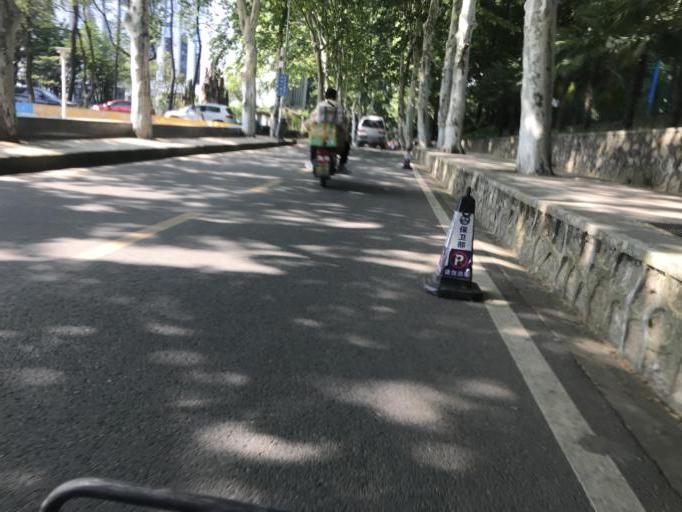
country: CN
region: Hubei
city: Shizishan
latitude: 30.5306
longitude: 114.3564
